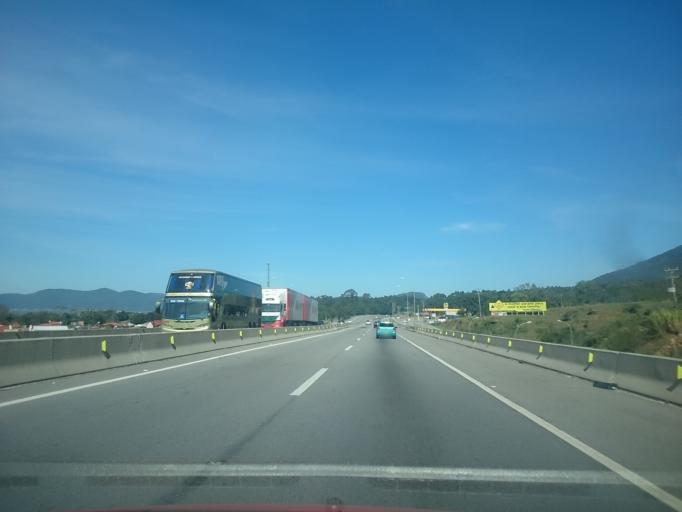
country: BR
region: Santa Catarina
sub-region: Palhoca
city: Palhoca
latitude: -27.7190
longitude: -48.6467
